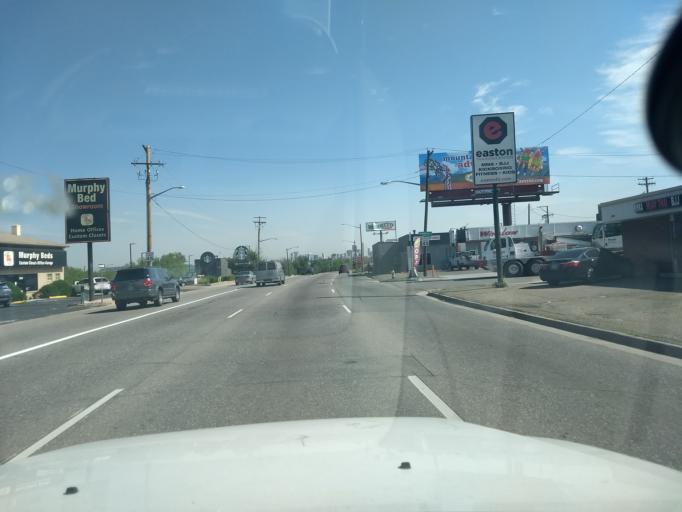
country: US
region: Colorado
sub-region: Arapahoe County
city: Englewood
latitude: 39.6926
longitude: -104.9925
